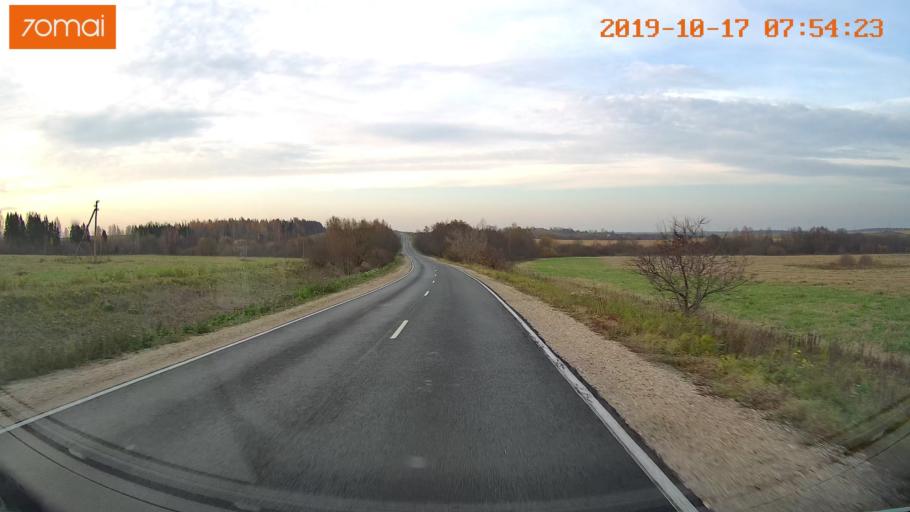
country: RU
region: Vladimir
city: Bavleny
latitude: 56.4504
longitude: 39.6067
